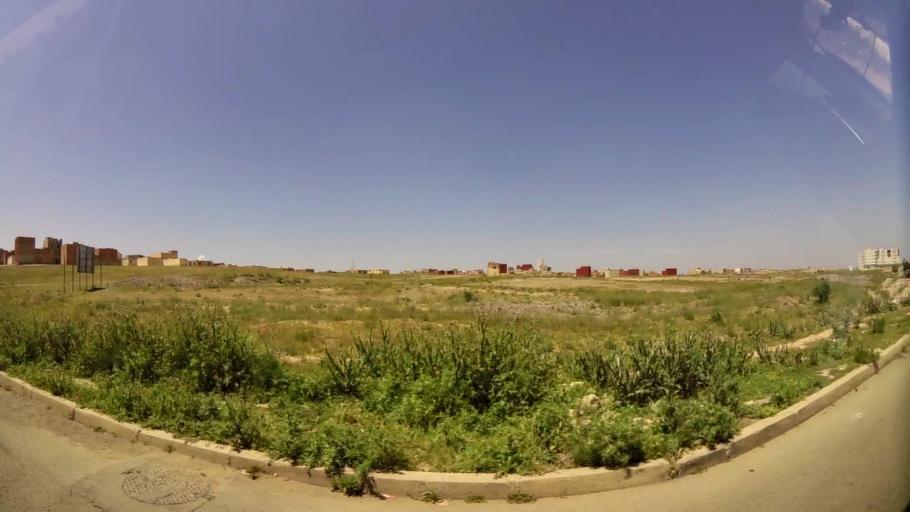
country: MA
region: Oriental
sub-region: Oujda-Angad
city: Oujda
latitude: 34.6854
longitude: -1.9499
